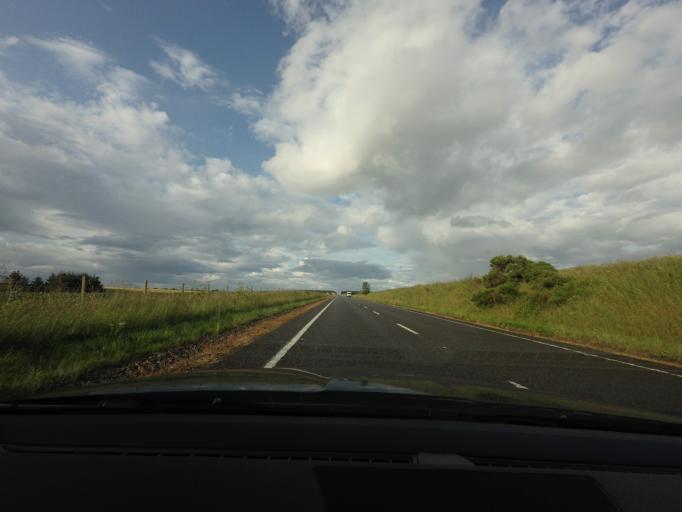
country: GB
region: Scotland
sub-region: Highland
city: Fortrose
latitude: 57.5410
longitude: -4.0137
